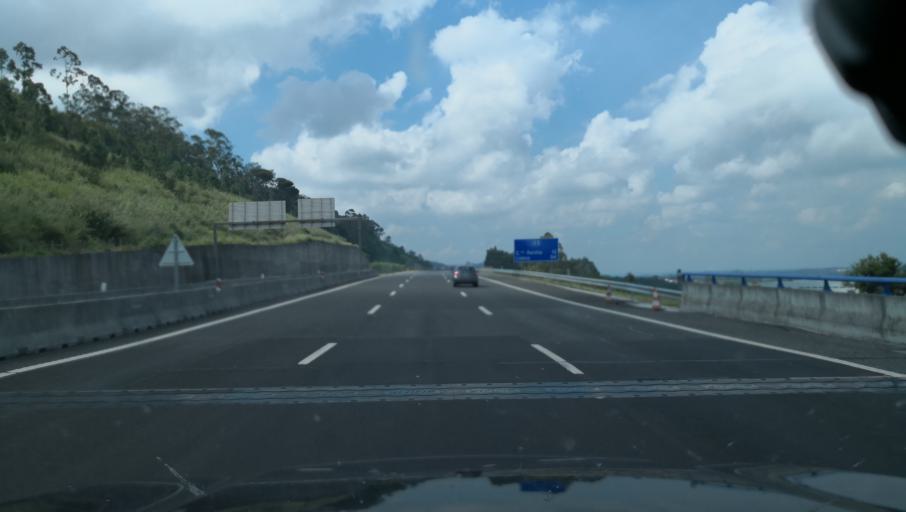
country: PT
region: Leiria
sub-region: Caldas da Rainha
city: Caldas da Rainha
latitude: 39.4929
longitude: -9.0937
